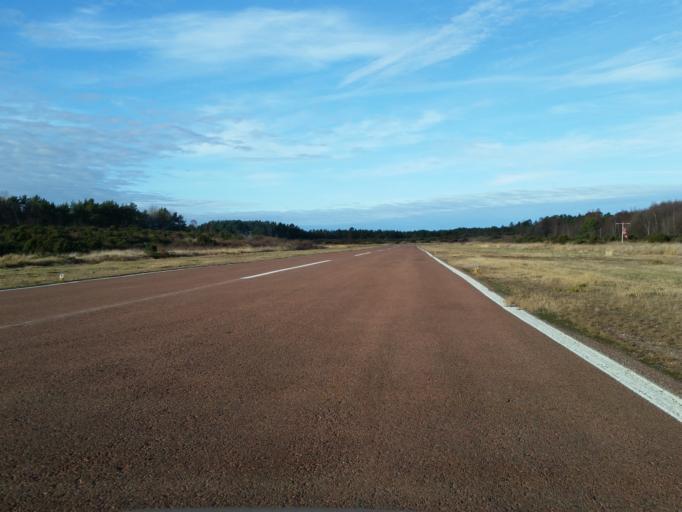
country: AX
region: Alands skaergard
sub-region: Kumlinge
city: Kumlinge
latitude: 60.2435
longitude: 20.8058
